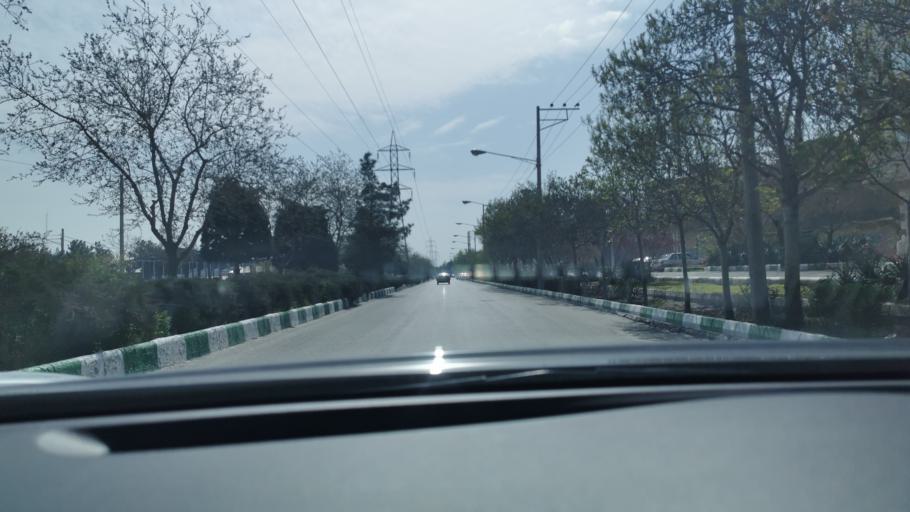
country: IR
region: Razavi Khorasan
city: Mashhad
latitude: 36.2821
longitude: 59.5457
